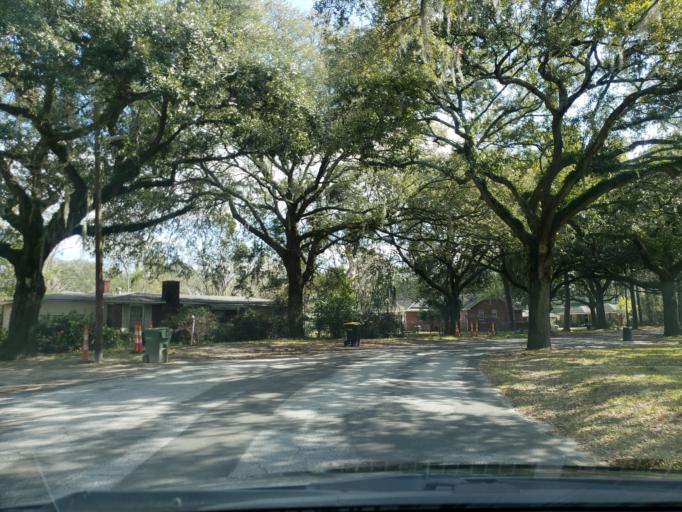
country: US
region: Georgia
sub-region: Chatham County
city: Savannah
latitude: 32.0269
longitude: -81.1075
